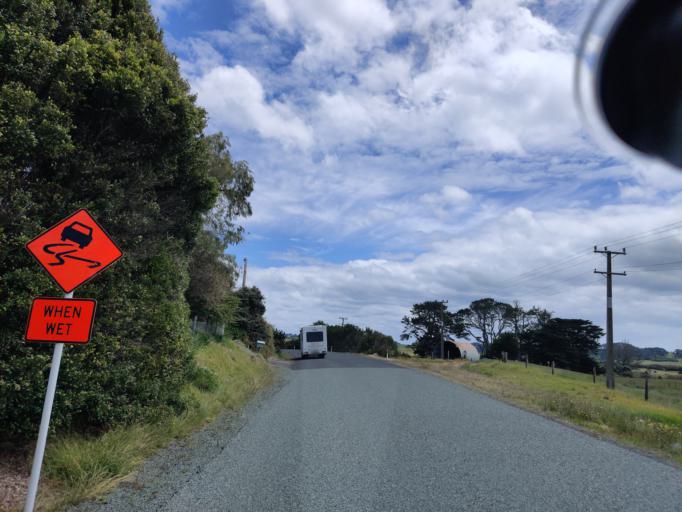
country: NZ
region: Northland
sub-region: Far North District
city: Kaitaia
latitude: -34.7733
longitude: 173.0903
